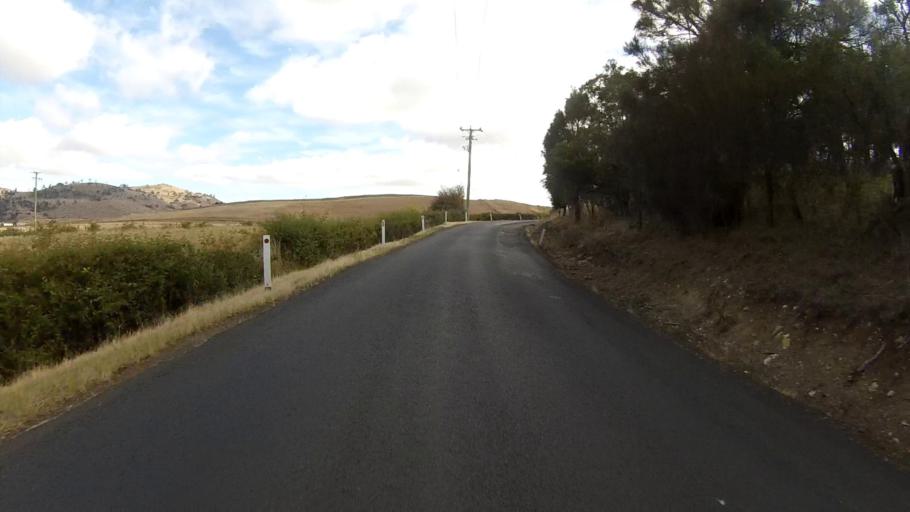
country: AU
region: Tasmania
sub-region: Brighton
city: Old Beach
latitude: -42.7491
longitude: 147.3006
